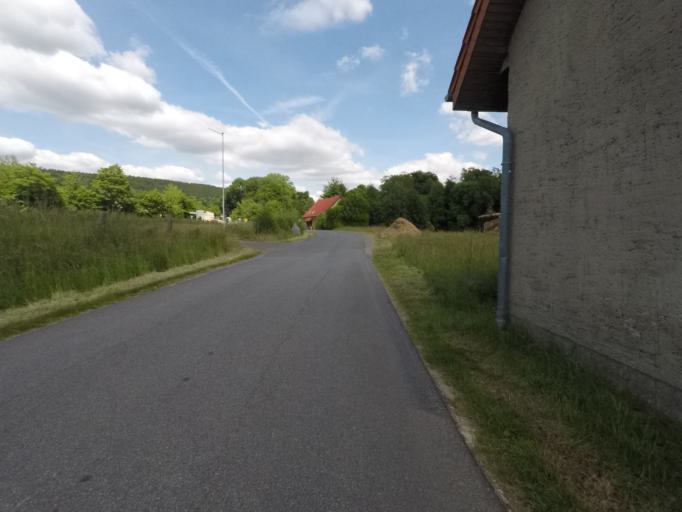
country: DE
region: North Rhine-Westphalia
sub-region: Regierungsbezirk Detmold
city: Rodinghausen
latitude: 52.2489
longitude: 8.4733
